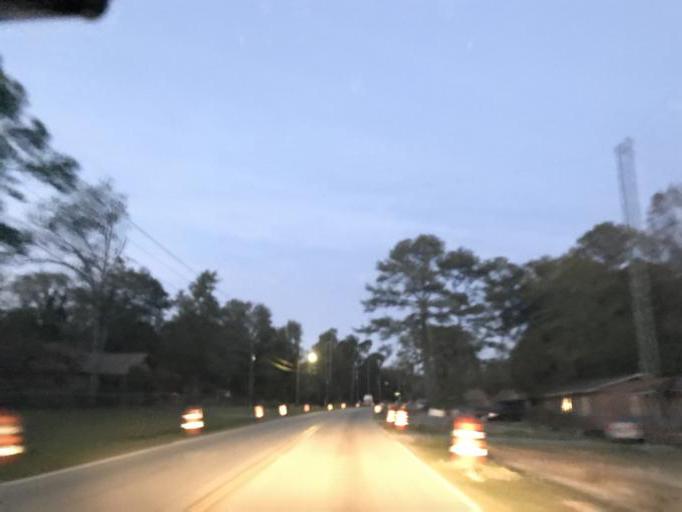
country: US
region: Georgia
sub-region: Bibb County
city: Macon
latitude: 32.8565
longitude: -83.5859
